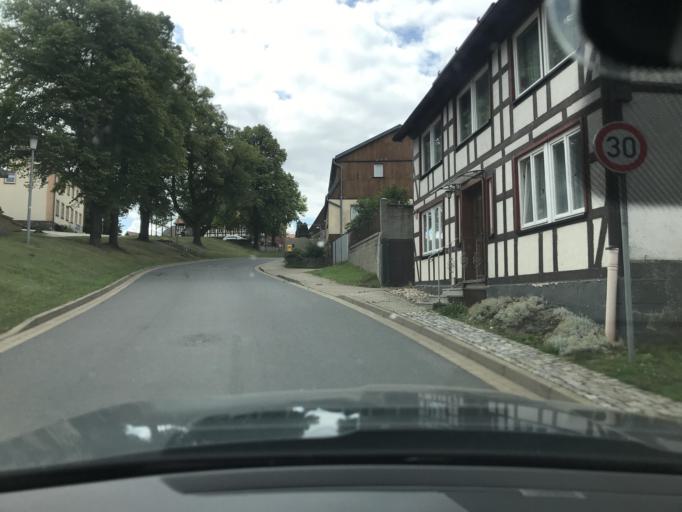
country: DE
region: Saxony-Anhalt
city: Friedrichsbrunn
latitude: 51.6157
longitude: 11.0485
